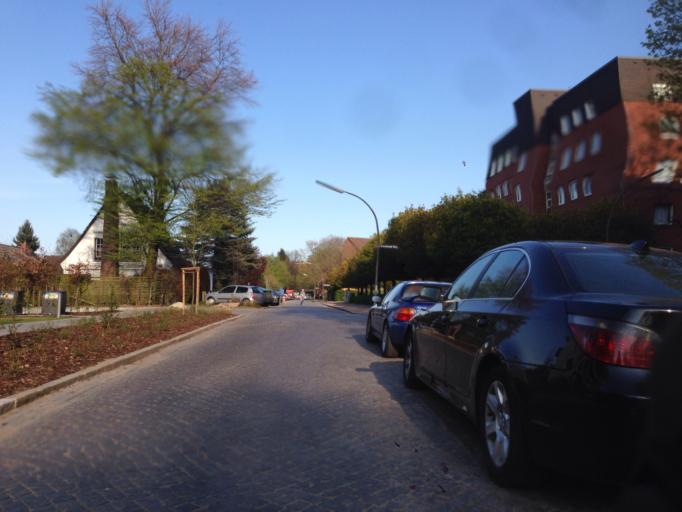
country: DE
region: Hamburg
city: Steilshoop
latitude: 53.5897
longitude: 10.0683
